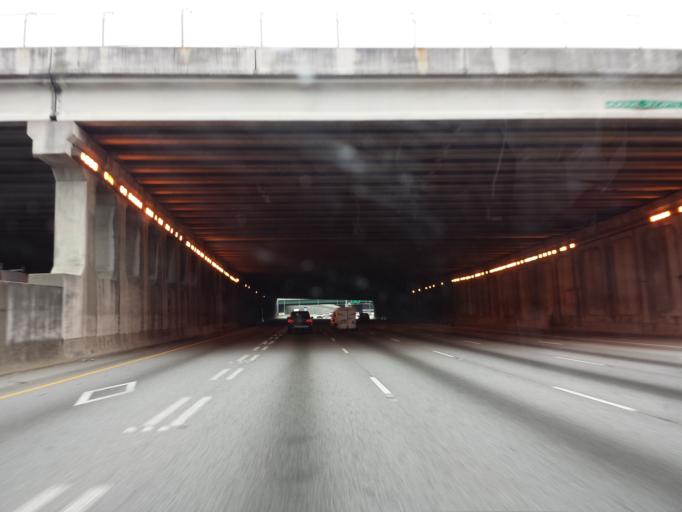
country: US
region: Georgia
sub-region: Fulton County
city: Atlanta
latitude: 33.7463
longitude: -84.3883
